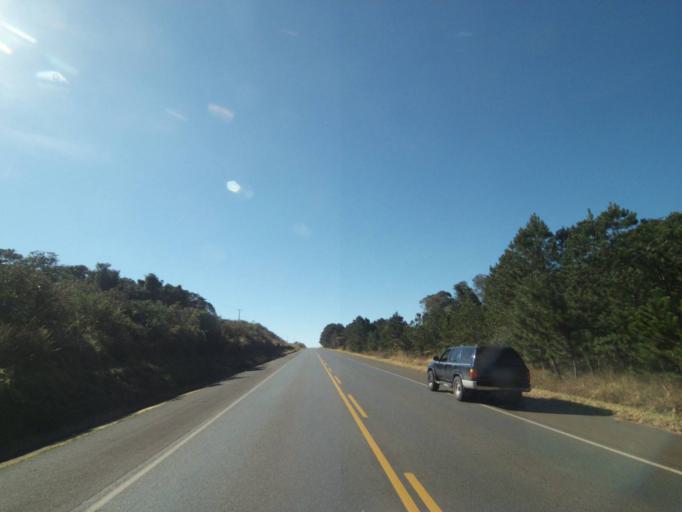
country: BR
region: Parana
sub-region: Tibagi
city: Tibagi
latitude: -24.3677
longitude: -50.3251
